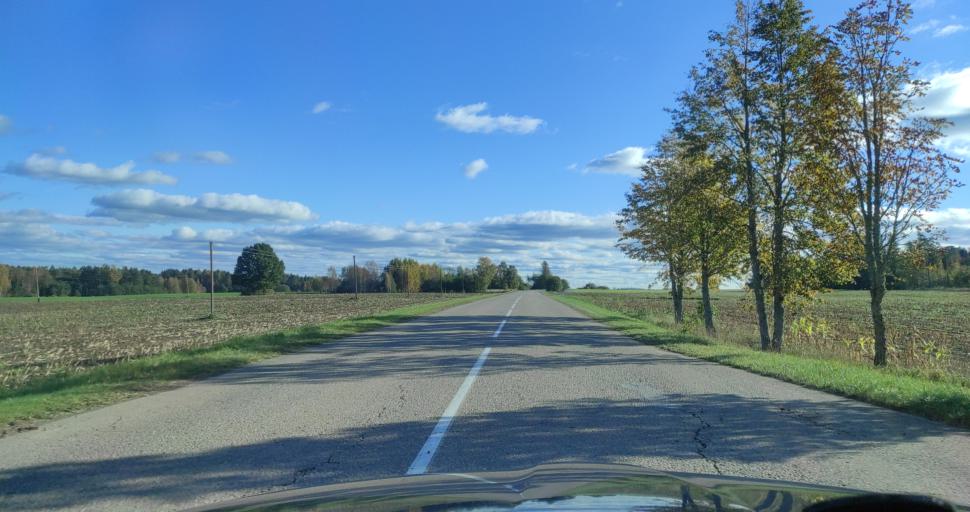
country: LV
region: Aizpute
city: Aizpute
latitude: 56.7732
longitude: 21.5237
